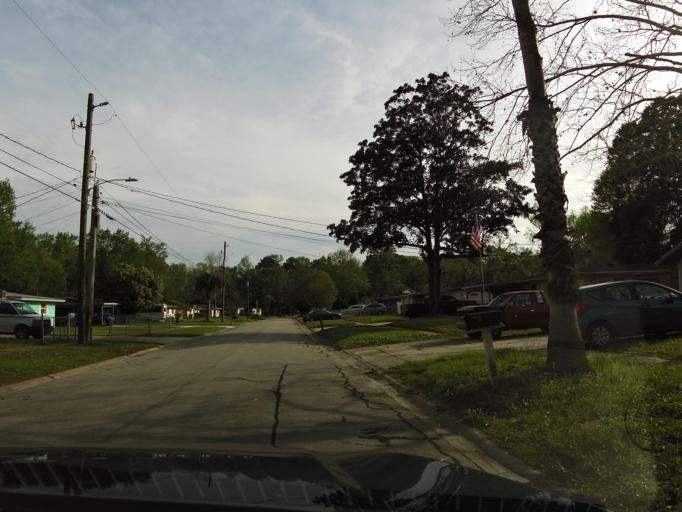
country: US
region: Florida
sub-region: Clay County
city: Bellair-Meadowbrook Terrace
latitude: 30.2390
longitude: -81.7588
